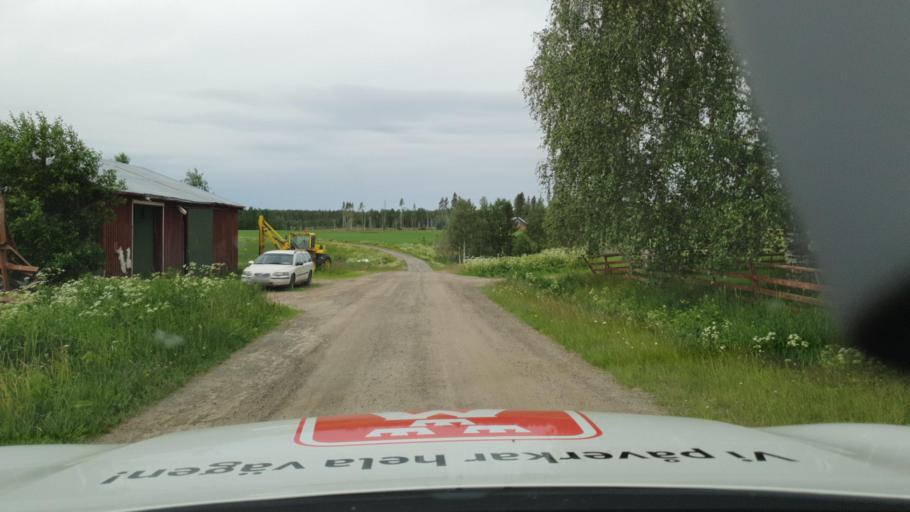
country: SE
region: Vaesterbotten
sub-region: Robertsfors Kommun
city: Robertsfors
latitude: 64.2853
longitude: 20.6629
